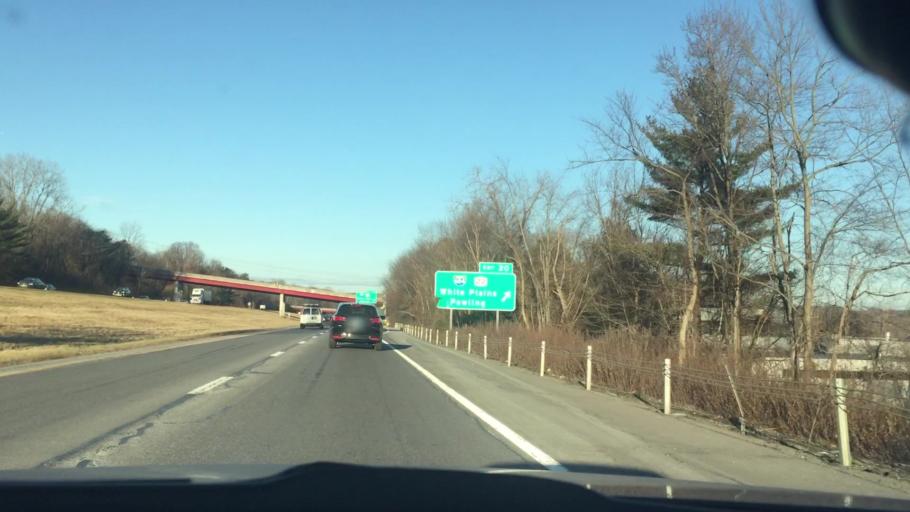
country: US
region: New York
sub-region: Putnam County
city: Peach Lake
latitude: 41.3874
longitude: -73.5911
